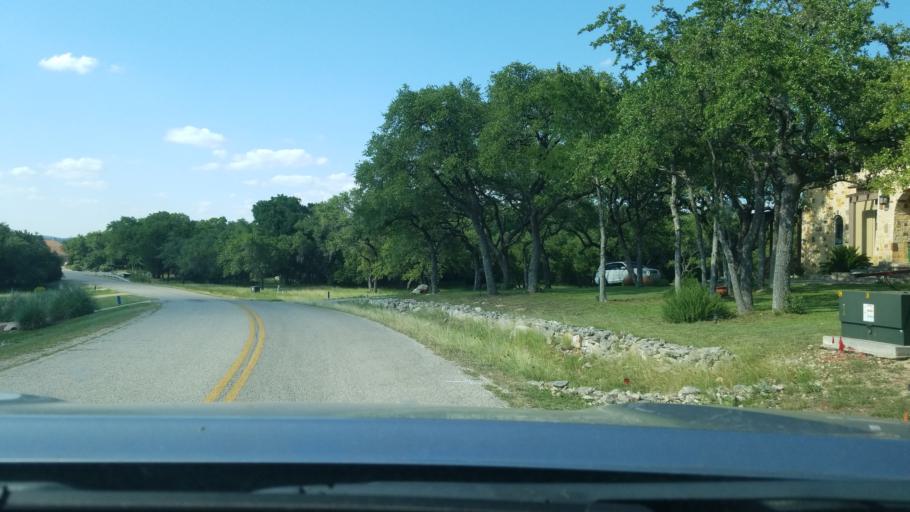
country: US
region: Texas
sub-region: Comal County
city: Bulverde
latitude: 29.8299
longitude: -98.3973
